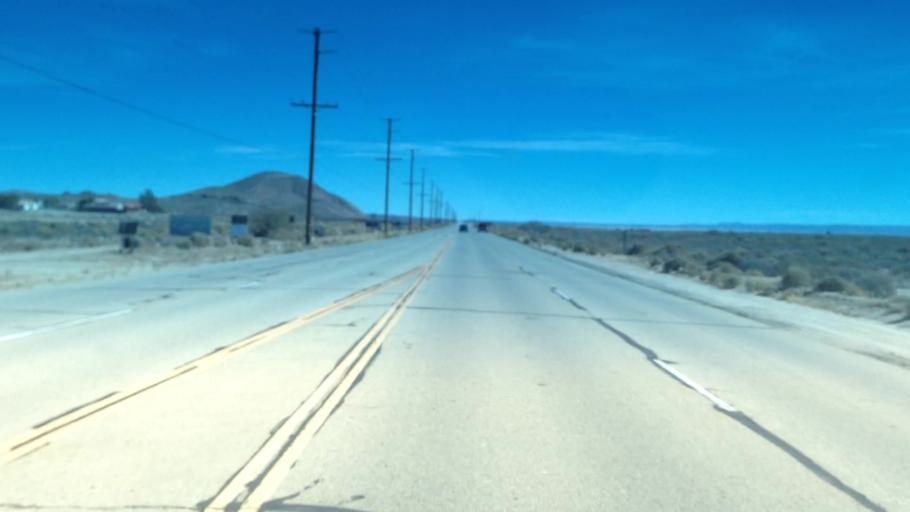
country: US
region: California
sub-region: Kern County
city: Rosamond
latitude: 34.8645
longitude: -118.1486
